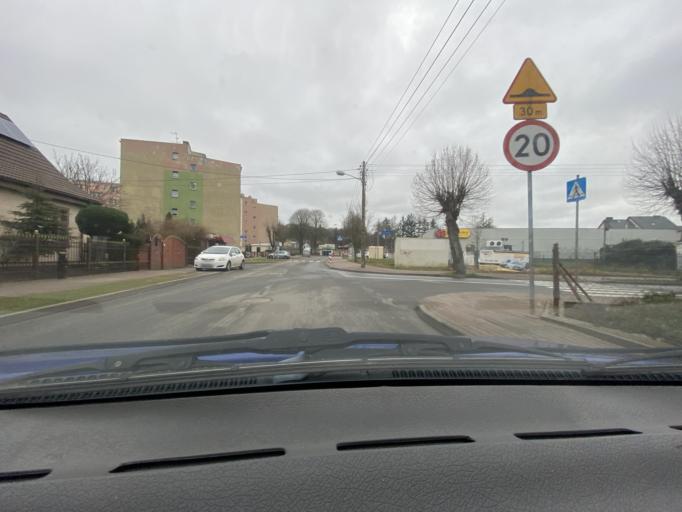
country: PL
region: West Pomeranian Voivodeship
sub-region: Powiat gryficki
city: Gryfice
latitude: 53.9145
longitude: 15.2073
